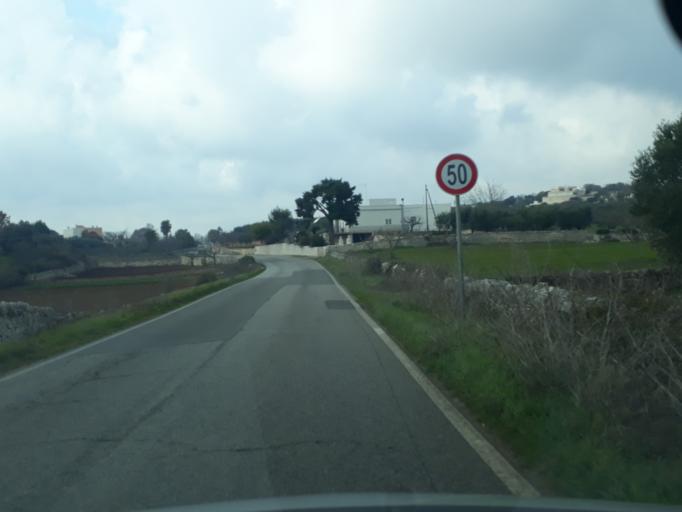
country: IT
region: Apulia
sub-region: Provincia di Bari
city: Locorotondo
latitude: 40.7537
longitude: 17.3644
